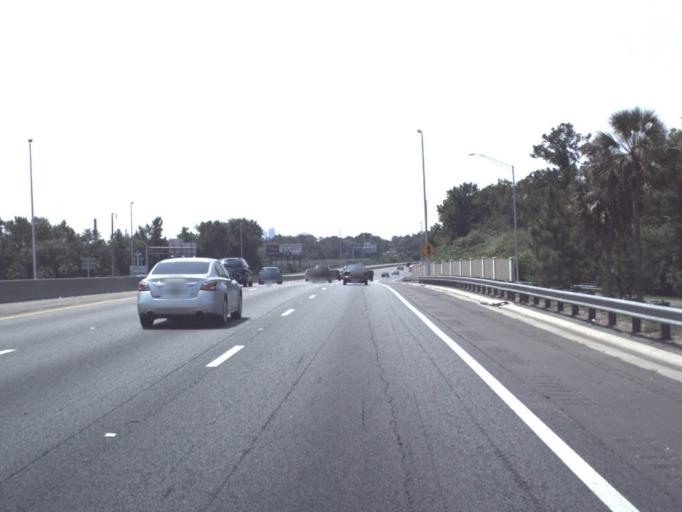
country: US
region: Florida
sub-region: Duval County
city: Jacksonville
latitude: 30.3921
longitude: -81.6681
